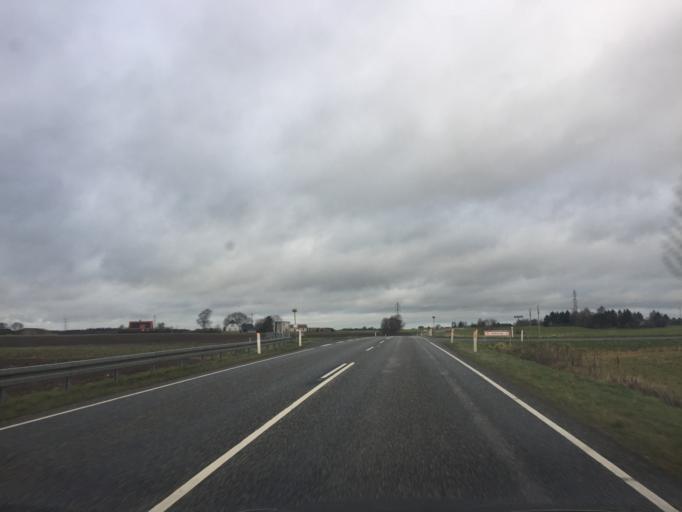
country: DK
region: Zealand
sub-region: Soro Kommune
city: Stenlille
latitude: 55.4886
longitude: 11.5729
